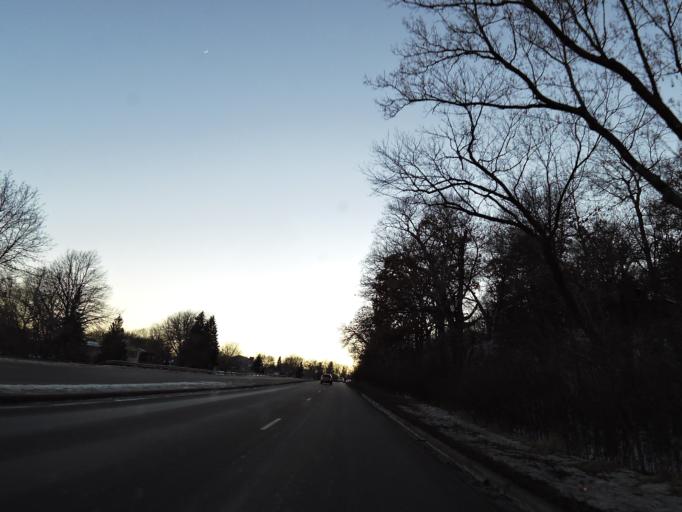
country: US
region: Minnesota
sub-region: Hennepin County
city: Bloomington
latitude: 44.8266
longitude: -93.3329
